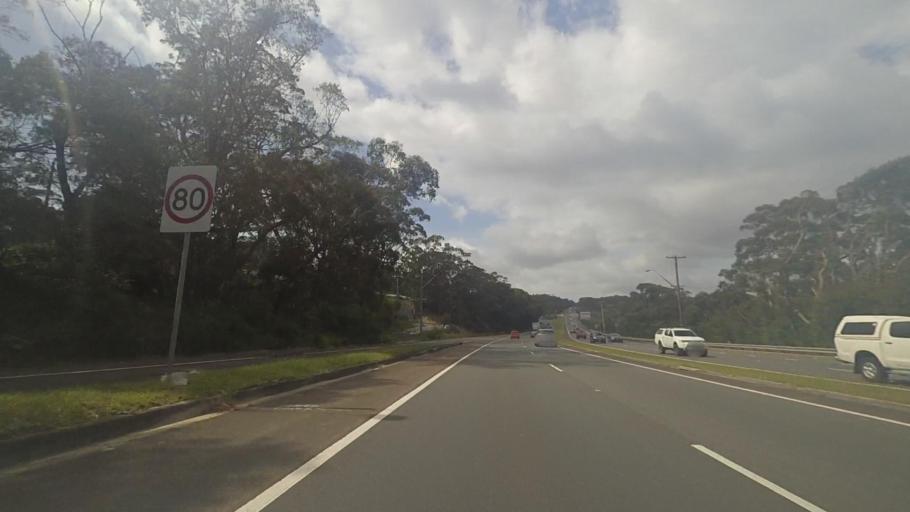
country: AU
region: New South Wales
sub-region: Wollongong
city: Helensburgh
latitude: -34.1370
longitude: 150.9945
